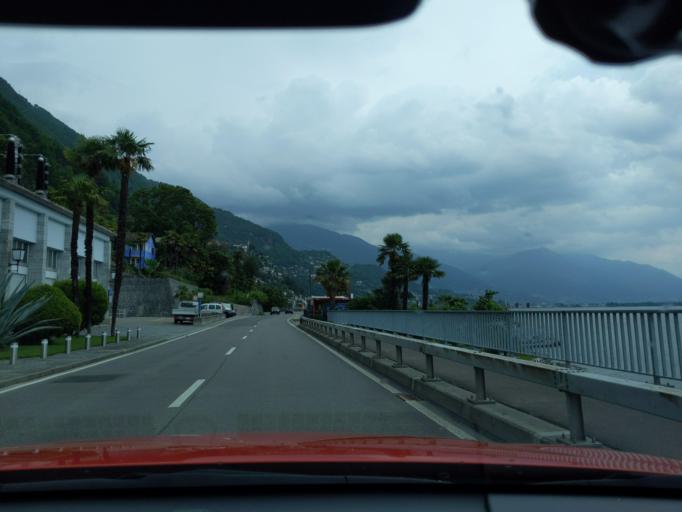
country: CH
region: Ticino
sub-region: Locarno District
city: Brissago
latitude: 46.1327
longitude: 8.7185
